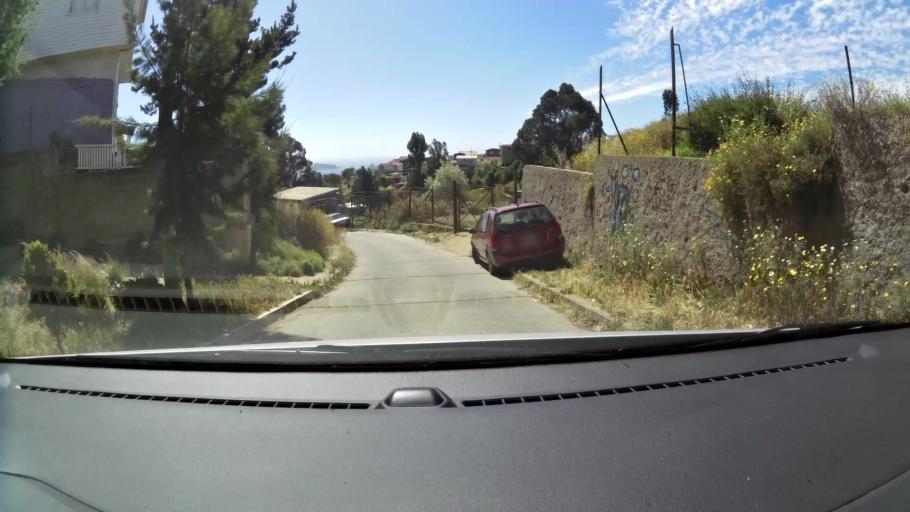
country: CL
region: Valparaiso
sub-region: Provincia de Valparaiso
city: Vina del Mar
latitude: -33.0416
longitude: -71.5791
